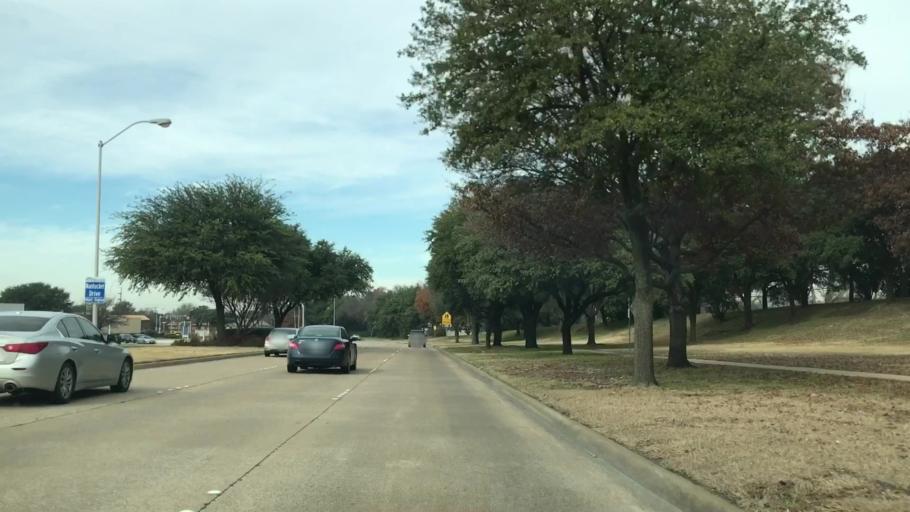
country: US
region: Texas
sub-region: Dallas County
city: Richardson
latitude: 32.9769
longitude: -96.7374
